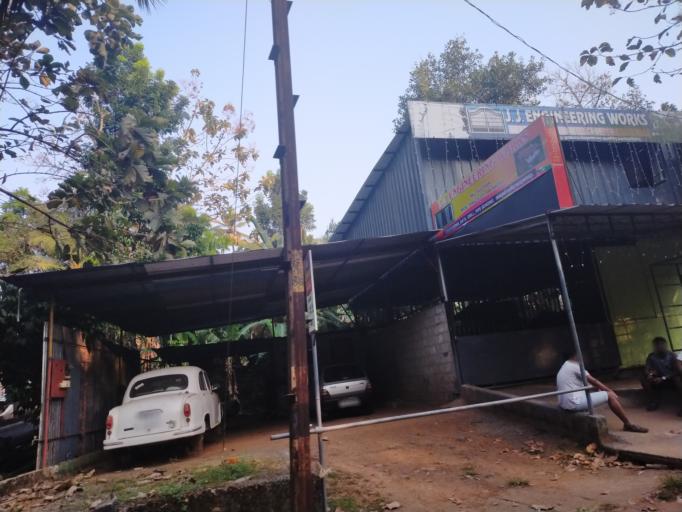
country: IN
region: Kerala
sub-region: Kottayam
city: Vaikam
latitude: 9.7533
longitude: 76.5042
